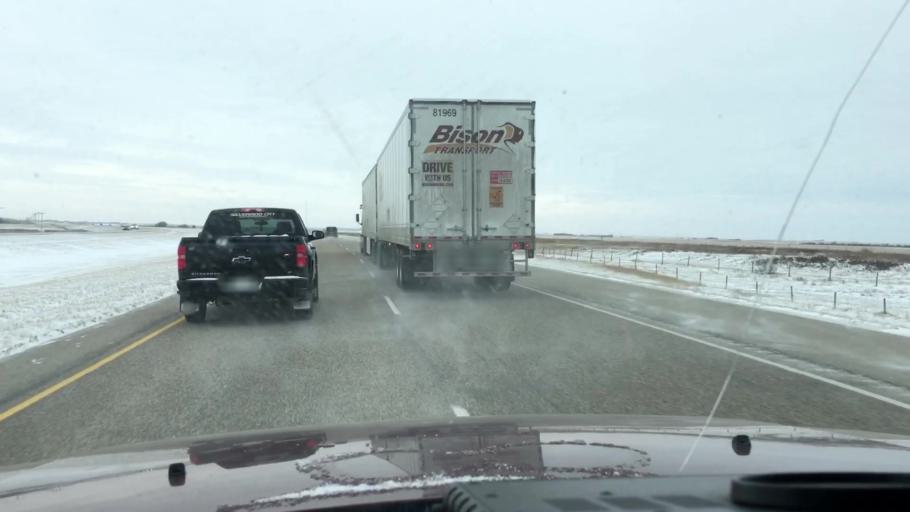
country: CA
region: Saskatchewan
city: Saskatoon
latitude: 51.6097
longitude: -106.4104
